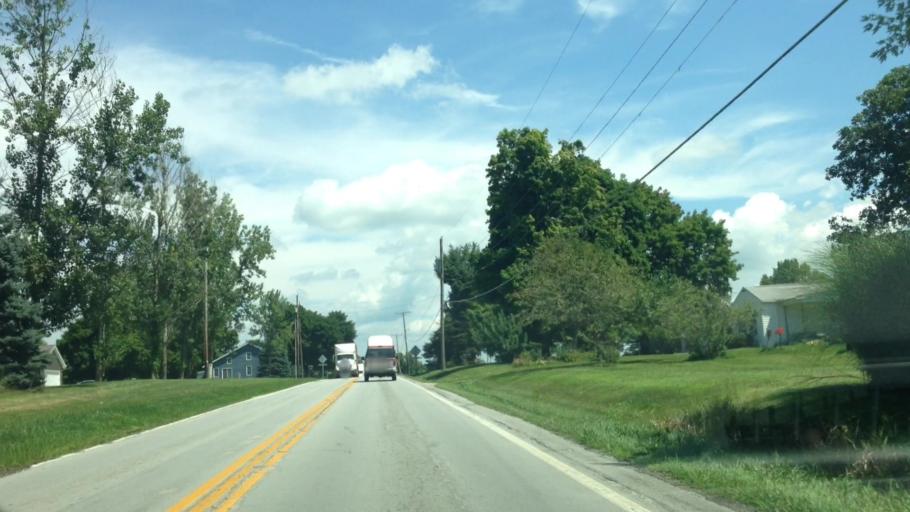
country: US
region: Ohio
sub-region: Wayne County
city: Smithville
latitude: 40.8742
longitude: -81.8416
